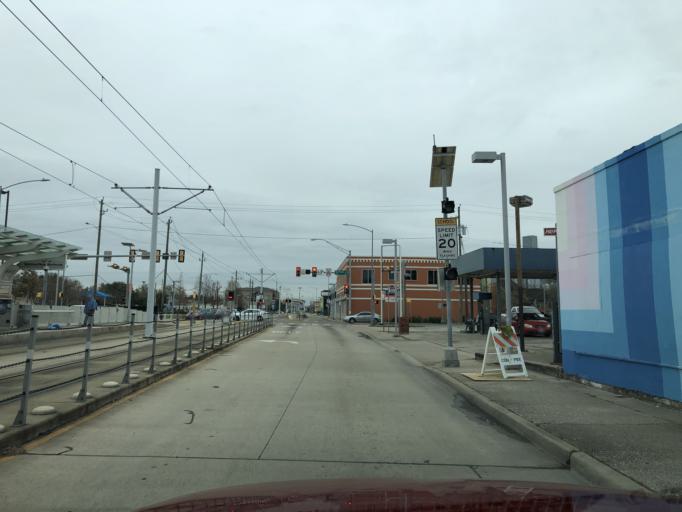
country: US
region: Texas
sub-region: Harris County
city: Houston
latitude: 29.7814
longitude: -95.3642
